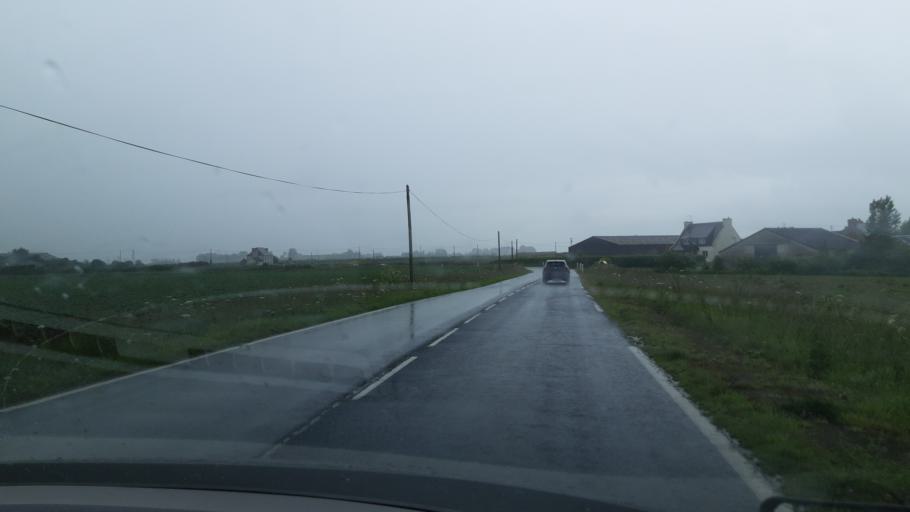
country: FR
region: Brittany
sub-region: Departement du Finistere
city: Saint-Pol-de-Leon
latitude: 48.6690
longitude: -4.0096
